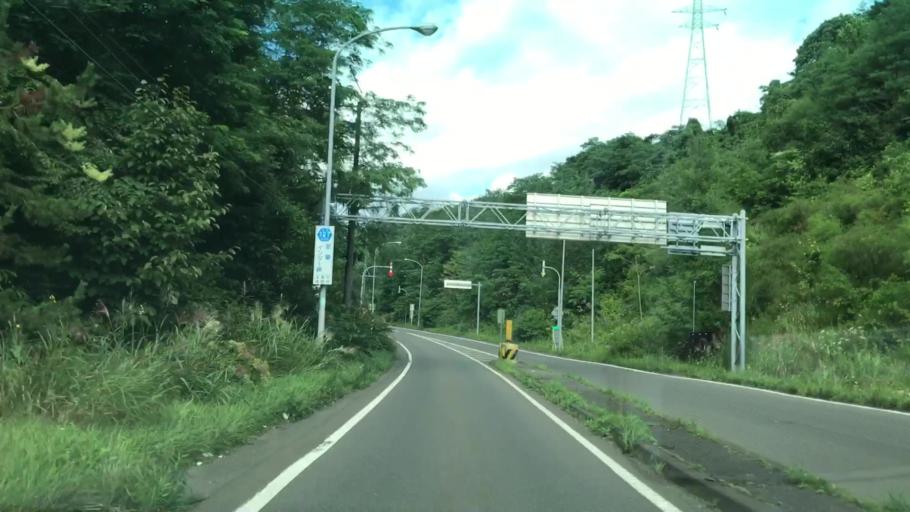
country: JP
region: Hokkaido
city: Muroran
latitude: 42.3657
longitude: 140.9523
